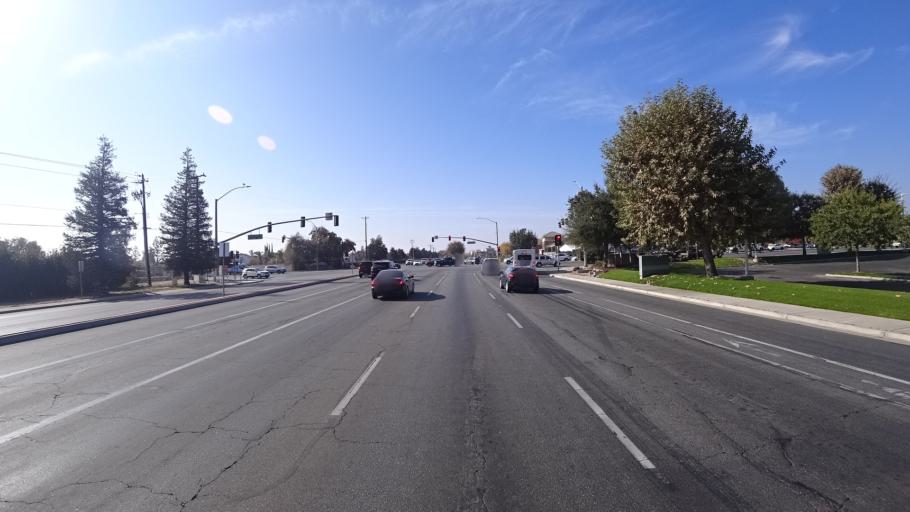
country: US
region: California
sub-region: Kern County
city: Greenacres
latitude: 35.3536
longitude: -119.1141
